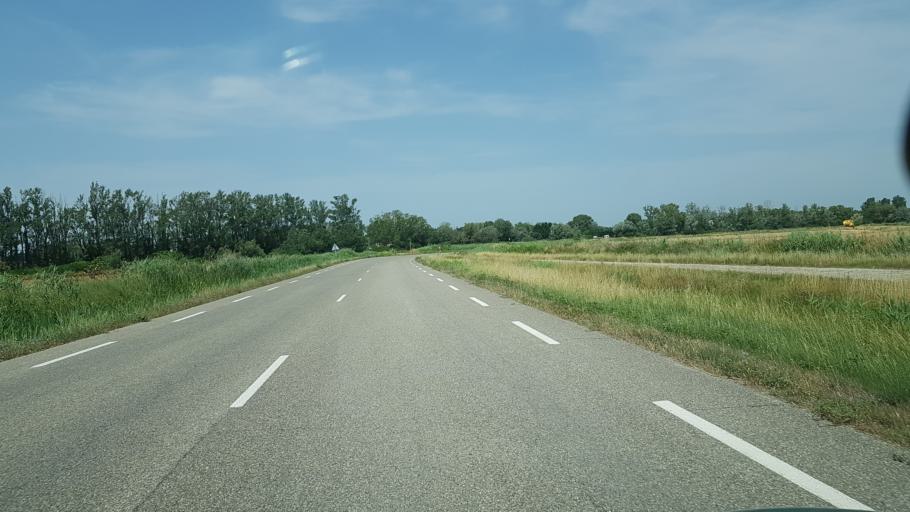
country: FR
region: Languedoc-Roussillon
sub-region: Departement du Gard
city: Saint-Gilles
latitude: 43.6059
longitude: 4.4823
